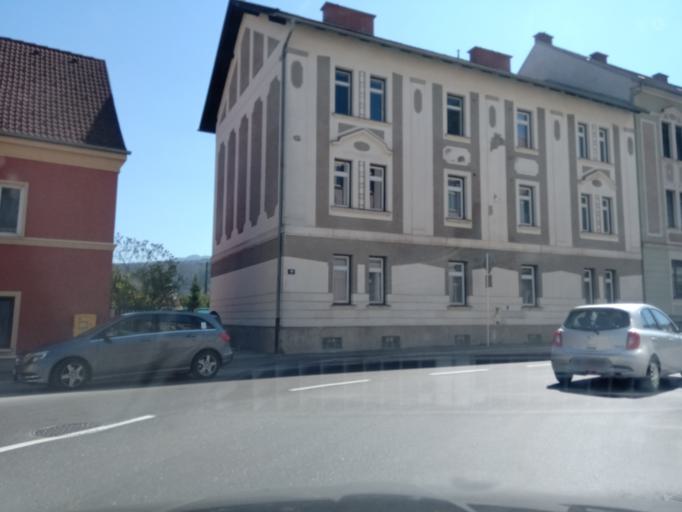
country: AT
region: Styria
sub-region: Politischer Bezirk Leoben
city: Leoben
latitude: 47.3744
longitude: 15.0832
